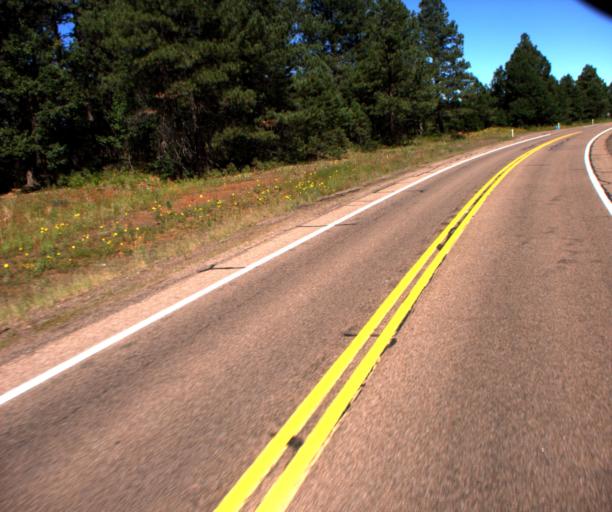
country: US
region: Arizona
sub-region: Navajo County
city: Pinetop-Lakeside
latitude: 34.0794
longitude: -109.8682
